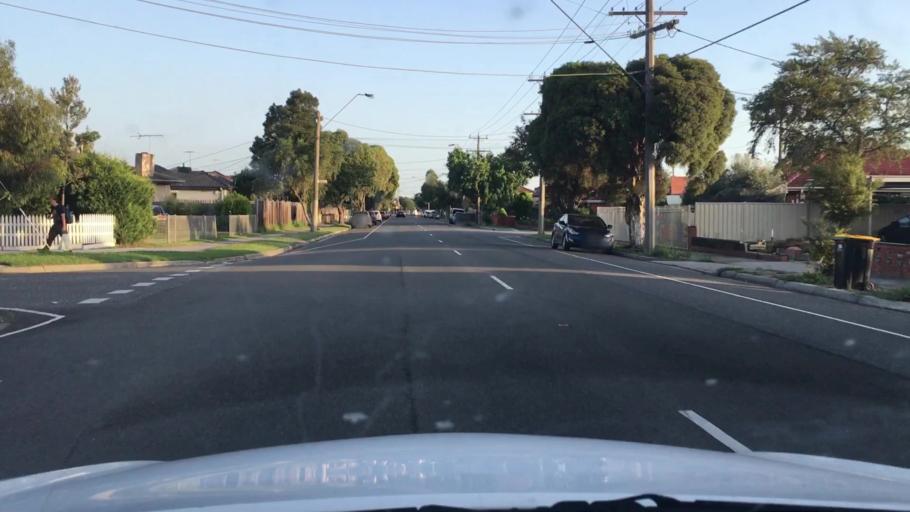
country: AU
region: Victoria
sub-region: Greater Dandenong
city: Noble Park
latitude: -37.9611
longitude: 145.1756
